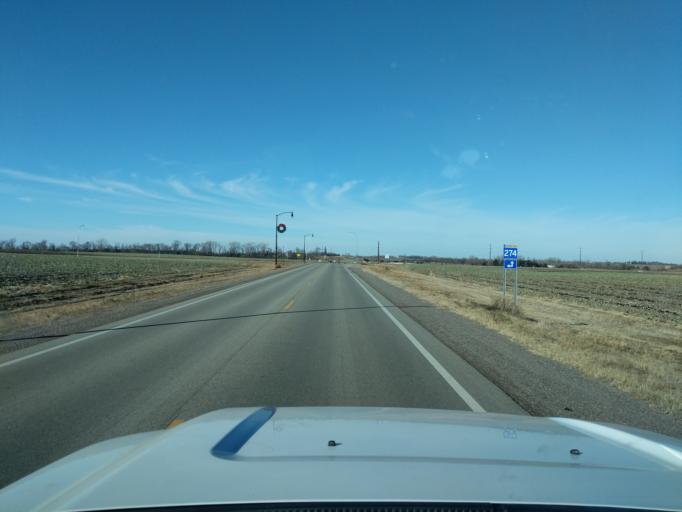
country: US
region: Minnesota
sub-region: Yellow Medicine County
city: Granite Falls
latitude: 44.7693
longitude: -95.5409
